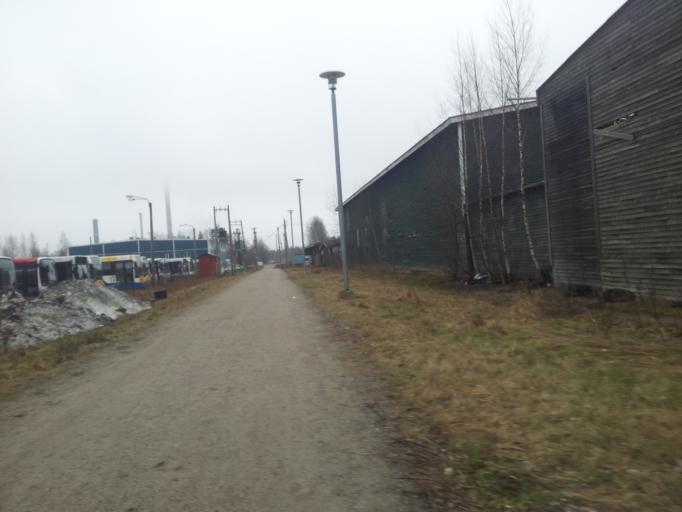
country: FI
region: Uusimaa
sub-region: Helsinki
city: Koukkuniemi
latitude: 60.1578
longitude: 24.7141
